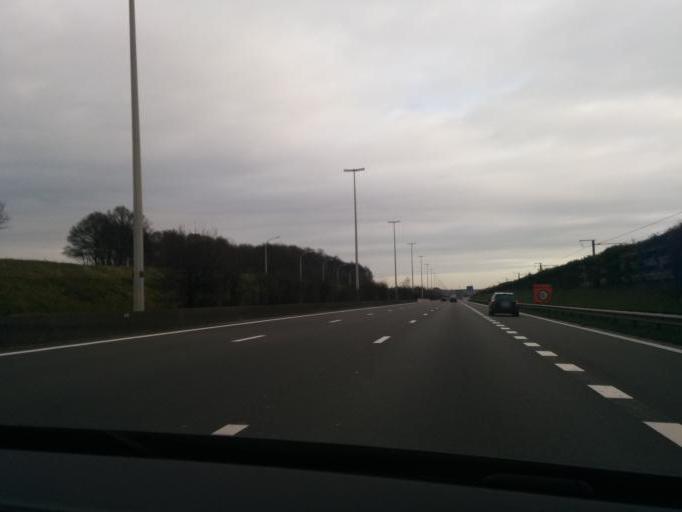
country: BE
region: Flanders
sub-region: Provincie Vlaams-Brabant
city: Boutersem
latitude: 50.8287
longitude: 4.8048
